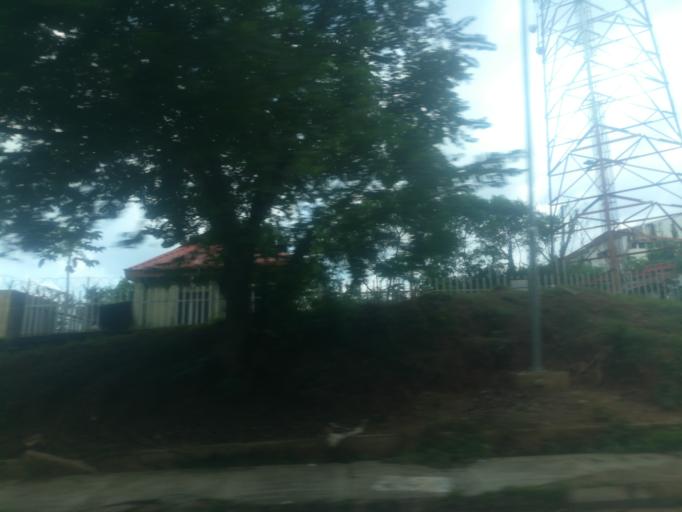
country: NG
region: Oyo
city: Ibadan
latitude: 7.4404
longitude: 3.8939
